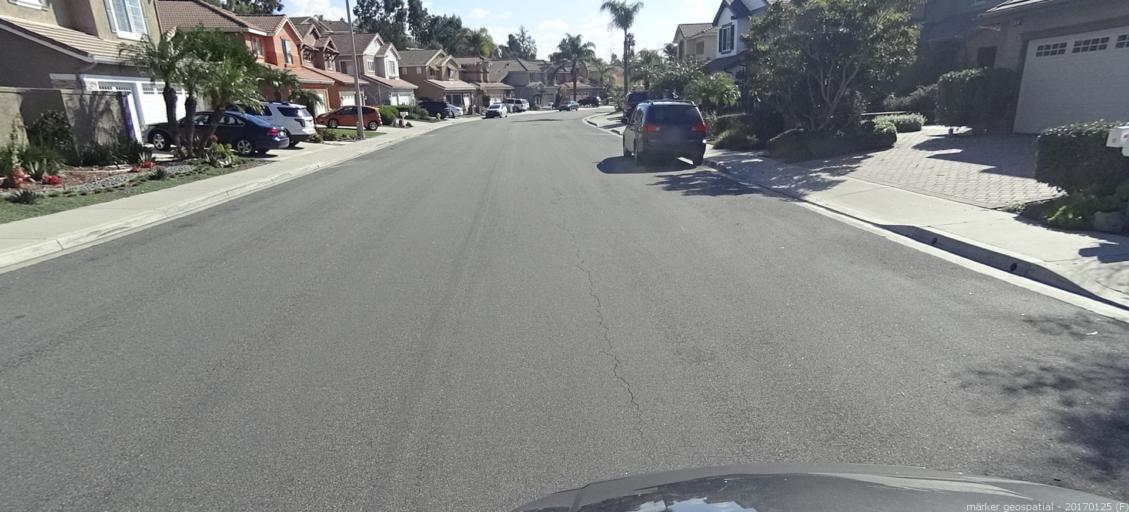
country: US
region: California
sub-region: Orange County
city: Foothill Ranch
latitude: 33.6893
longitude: -117.6550
